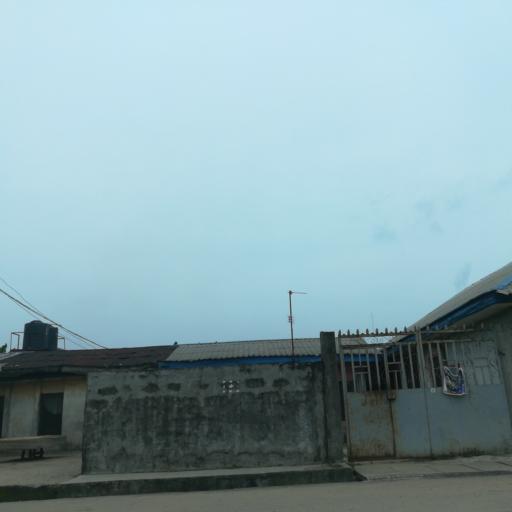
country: NG
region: Rivers
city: Port Harcourt
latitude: 4.8220
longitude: 7.0613
